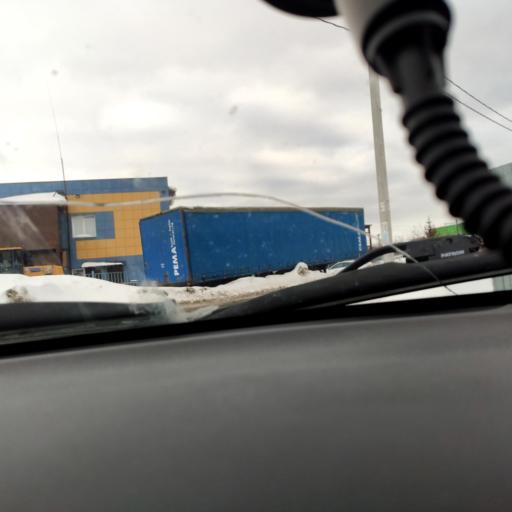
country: RU
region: Tatarstan
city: Osinovo
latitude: 55.8992
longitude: 48.9641
